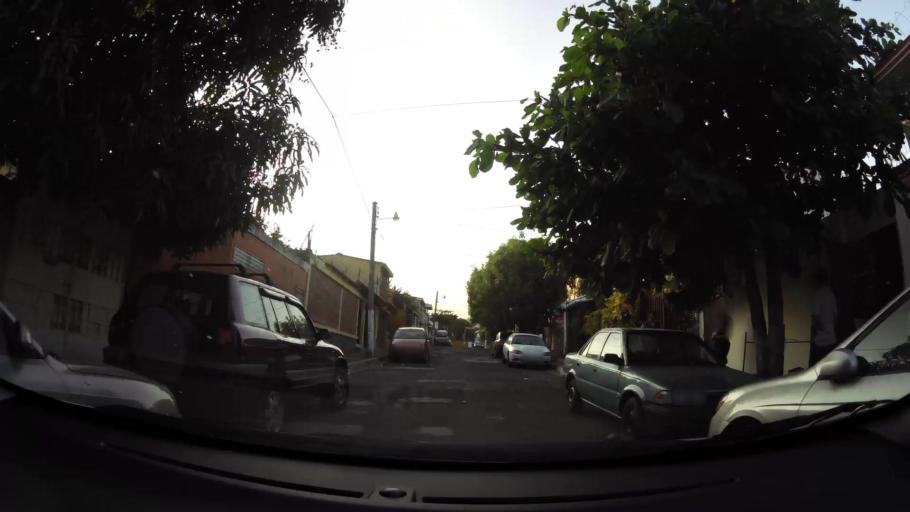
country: SV
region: San Salvador
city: Cuscatancingo
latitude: 13.7147
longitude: -89.1975
